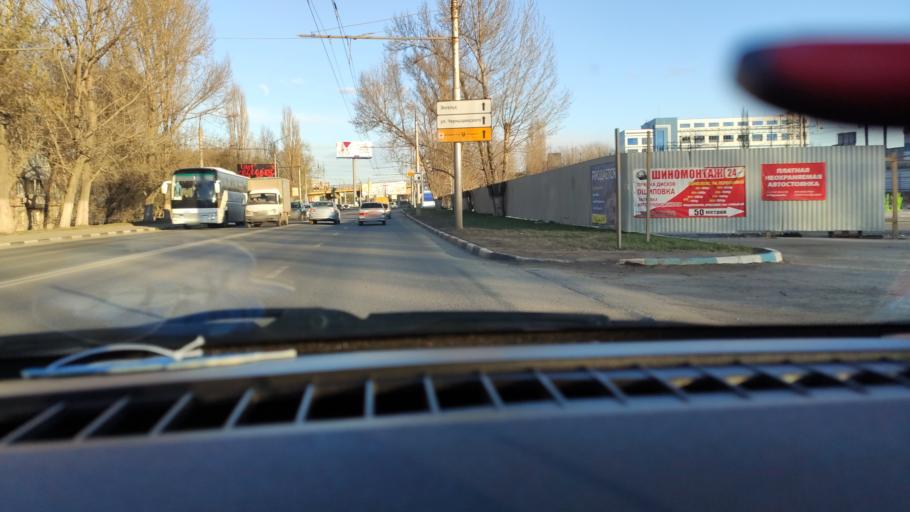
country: RU
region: Saratov
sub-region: Saratovskiy Rayon
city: Saratov
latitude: 51.5810
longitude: 45.9748
